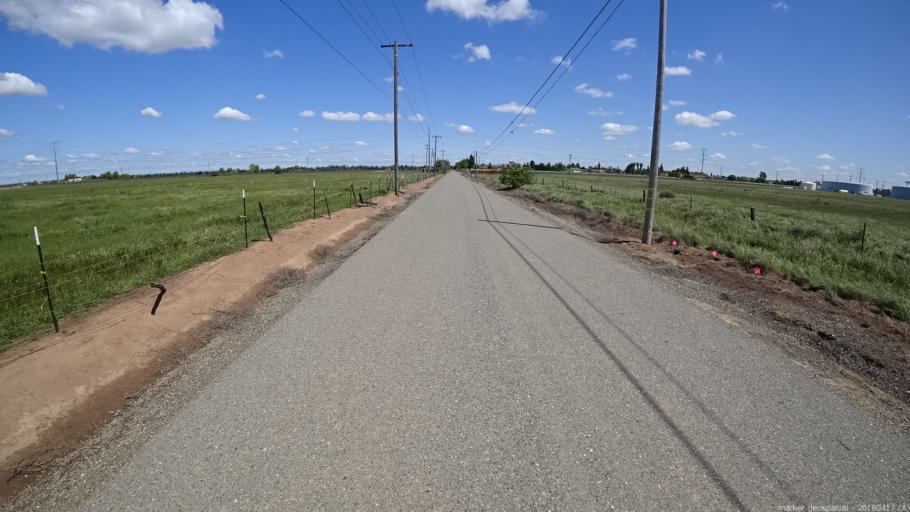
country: US
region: California
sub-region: Sacramento County
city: Laguna
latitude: 38.4342
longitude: -121.4610
